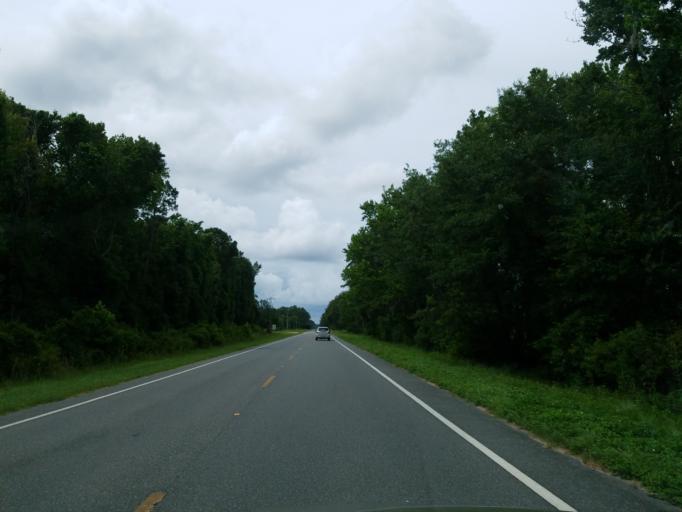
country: US
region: Florida
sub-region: Alachua County
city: High Springs
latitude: 29.8937
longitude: -82.4951
